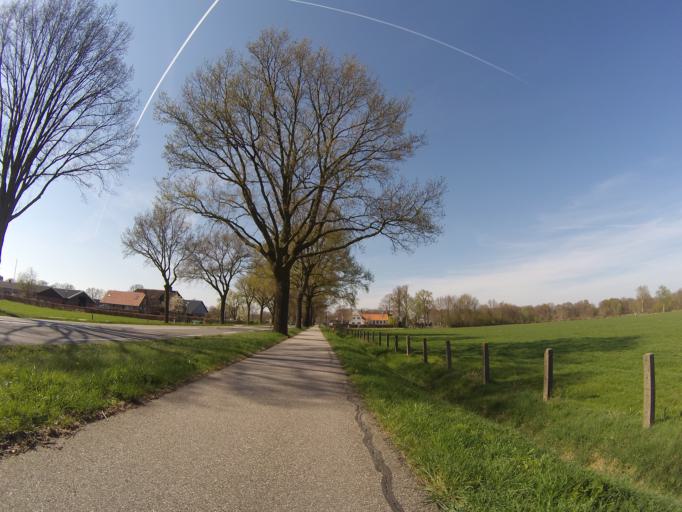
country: NL
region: Gelderland
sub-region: Gemeente Ede
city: Ederveen
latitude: 52.0611
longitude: 5.5567
